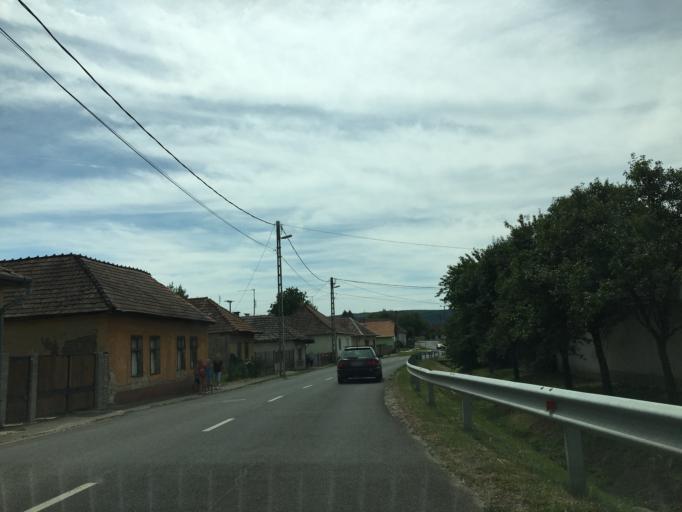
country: HU
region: Komarom-Esztergom
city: Esztergom
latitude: 47.8845
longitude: 18.7775
